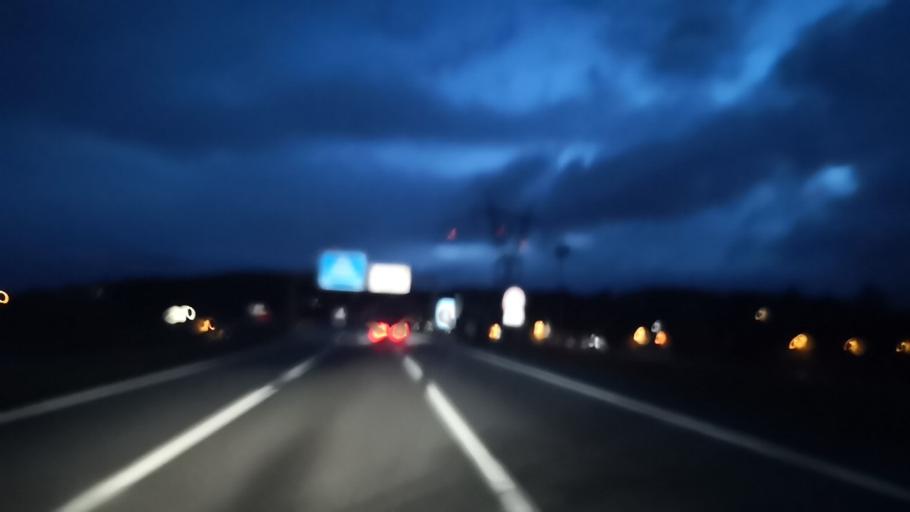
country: PT
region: Braga
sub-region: Guimaraes
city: Candoso
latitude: 41.4378
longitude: -8.3310
